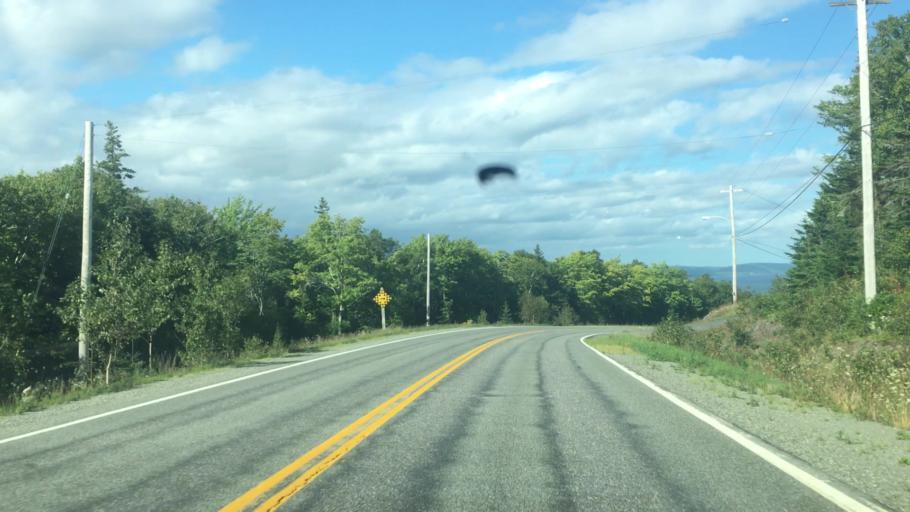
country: CA
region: Nova Scotia
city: Sydney
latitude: 45.8631
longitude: -60.6253
